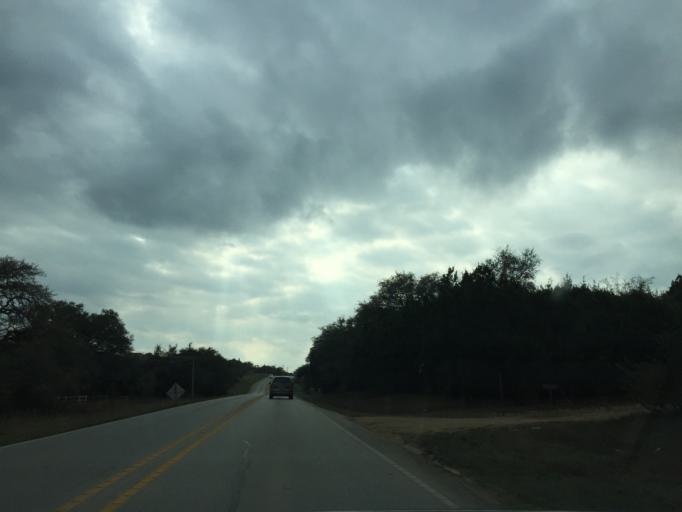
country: US
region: Texas
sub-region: Hays County
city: Dripping Springs
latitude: 30.1495
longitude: -97.9798
